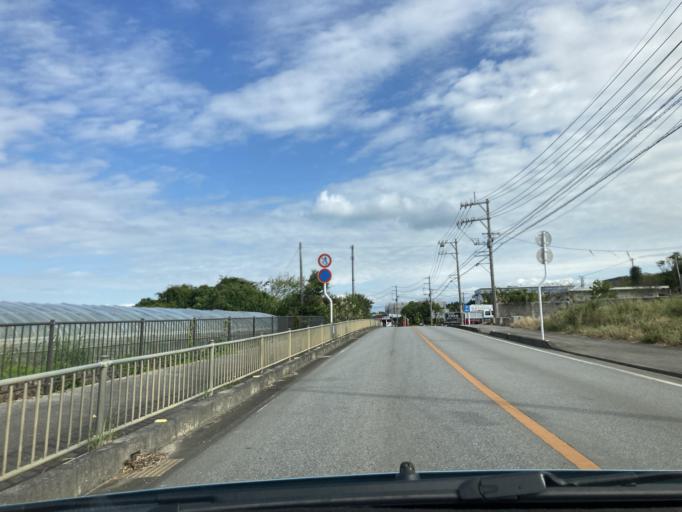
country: JP
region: Okinawa
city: Nago
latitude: 26.6960
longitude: 127.9463
